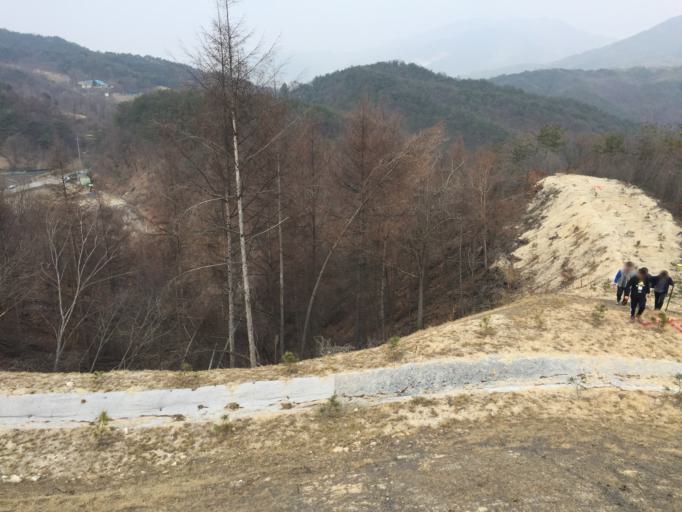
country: KR
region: Gangwon-do
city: Wonju
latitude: 37.1928
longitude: 127.8689
